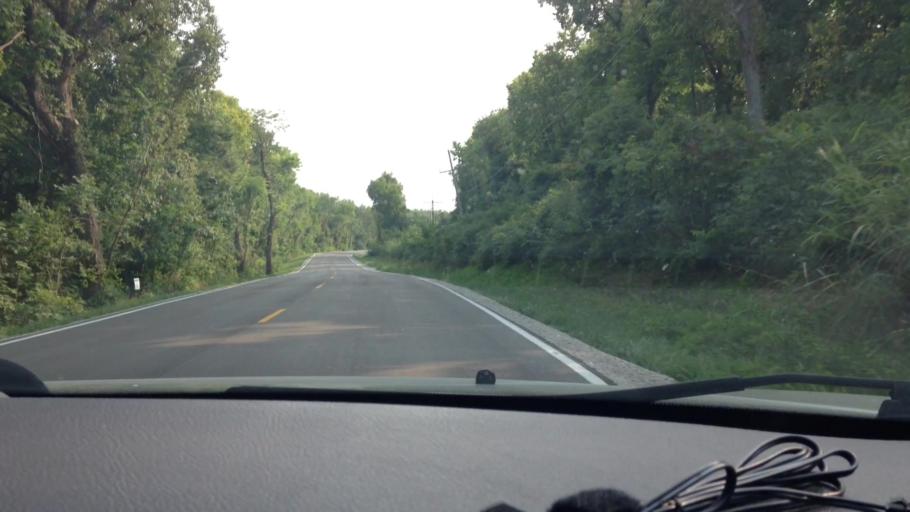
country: US
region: Missouri
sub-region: Platte County
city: Platte City
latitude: 39.3872
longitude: -94.7805
